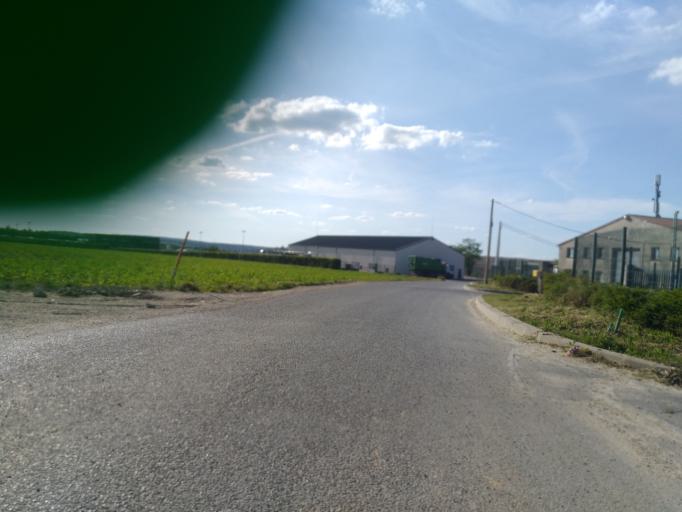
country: FR
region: Ile-de-France
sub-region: Departement des Yvelines
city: Thiverval-Grignon
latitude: 48.8320
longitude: 1.9297
